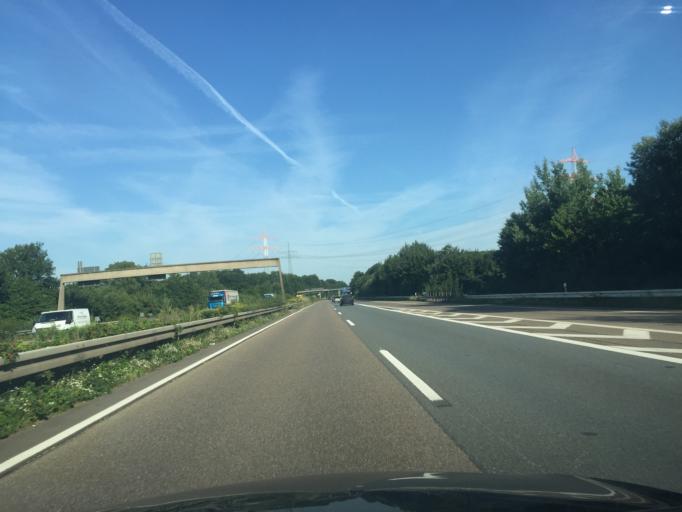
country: DE
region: North Rhine-Westphalia
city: Witten
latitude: 51.4658
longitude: 7.4097
